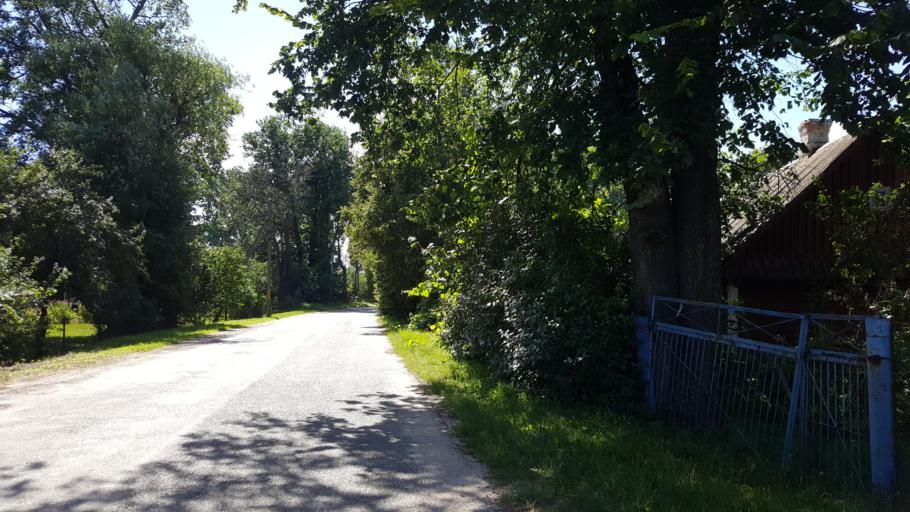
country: BY
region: Brest
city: Kobryn
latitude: 52.2976
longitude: 24.3421
